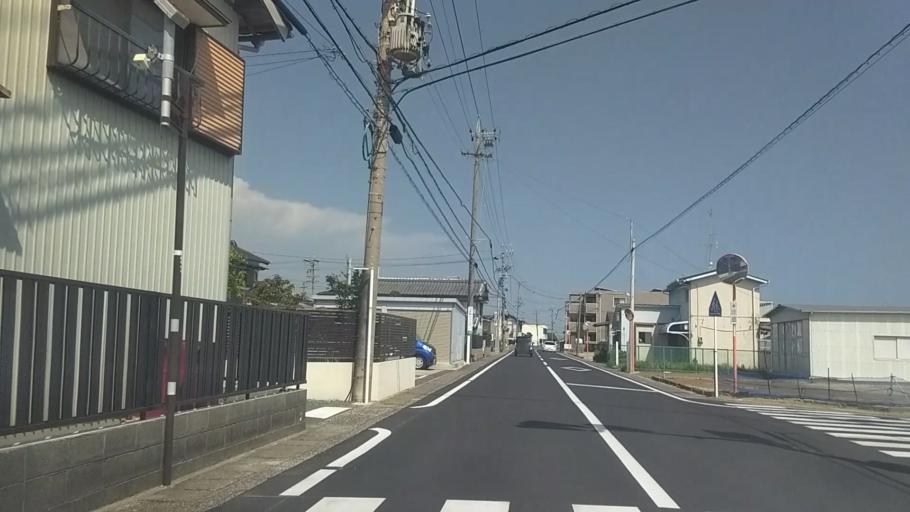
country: JP
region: Shizuoka
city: Hamamatsu
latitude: 34.6815
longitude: 137.6877
